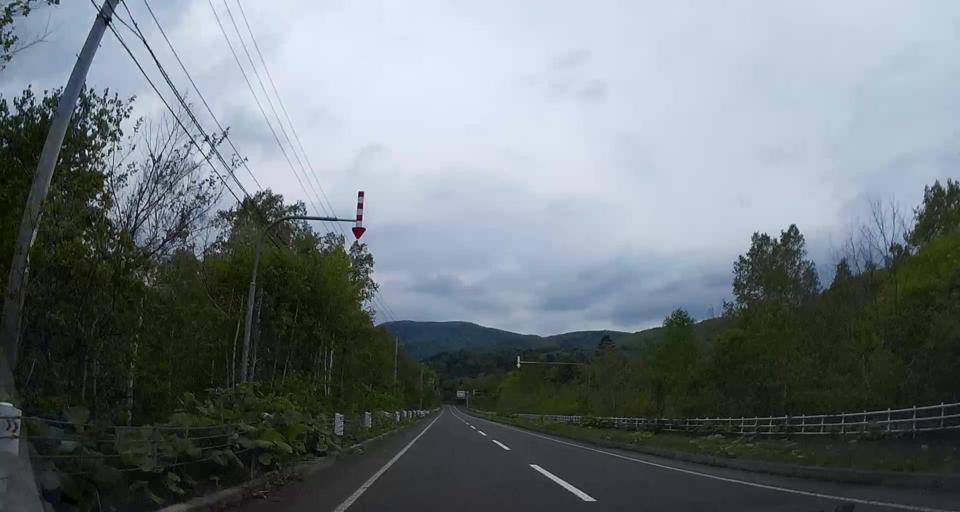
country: JP
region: Hokkaido
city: Shiraoi
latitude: 42.6753
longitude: 141.0994
